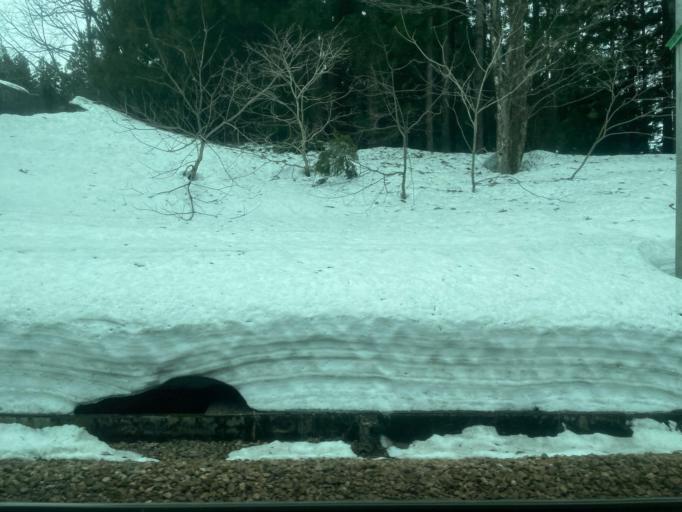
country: JP
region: Niigata
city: Shiozawa
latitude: 36.9257
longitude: 138.8525
